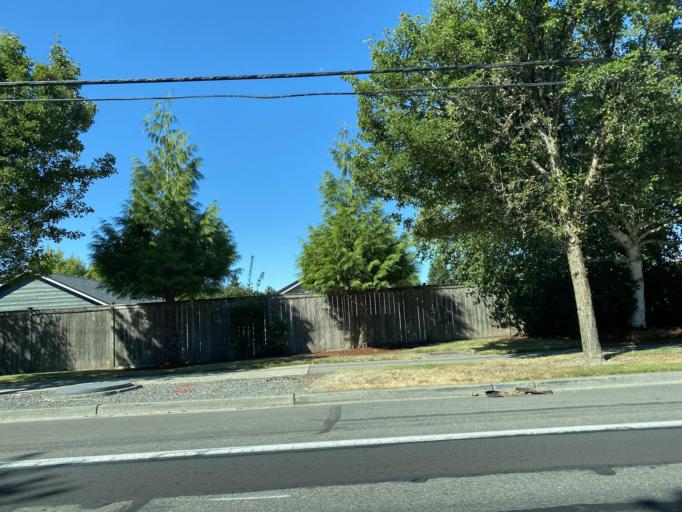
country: US
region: Washington
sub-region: Thurston County
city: Tumwater
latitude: 47.0053
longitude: -122.8652
